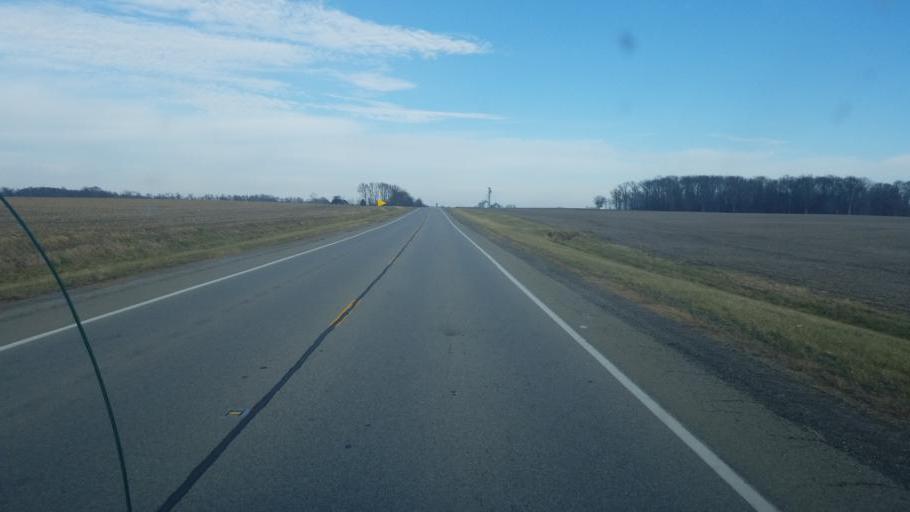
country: US
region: Illinois
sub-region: White County
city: Carmi
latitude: 38.1337
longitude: -88.0963
